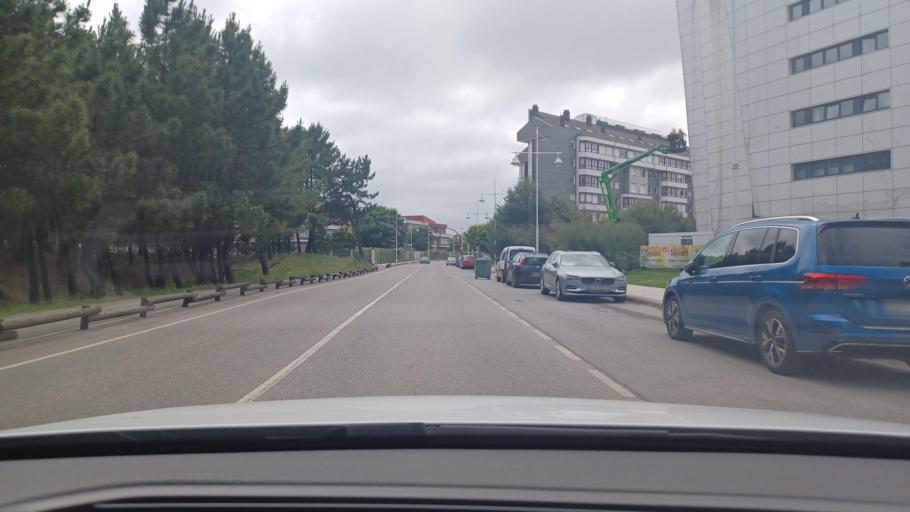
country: ES
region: Asturias
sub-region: Province of Asturias
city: Aviles
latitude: 43.5797
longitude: -5.9483
